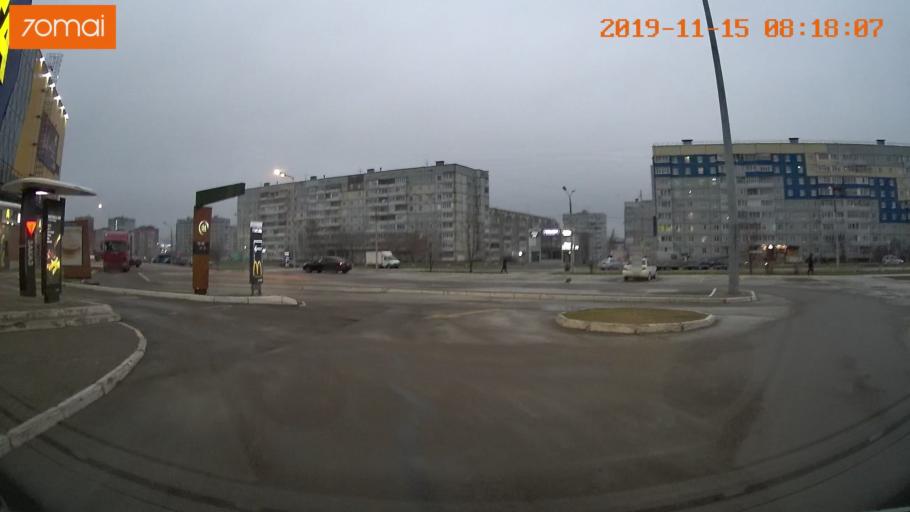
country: RU
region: Vologda
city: Cherepovets
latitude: 59.0926
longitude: 37.9185
